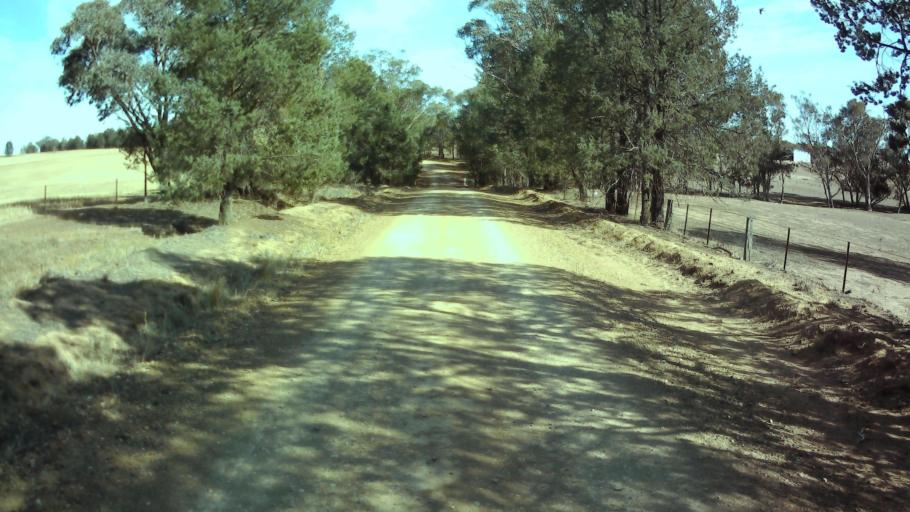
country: AU
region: New South Wales
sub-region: Weddin
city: Grenfell
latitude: -33.7652
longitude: 148.0450
